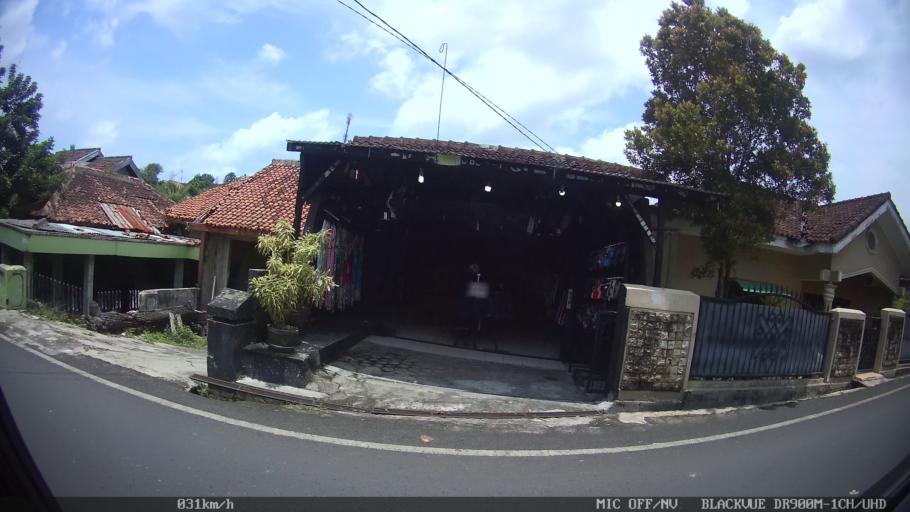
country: ID
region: Lampung
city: Bandarlampung
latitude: -5.4117
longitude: 105.2427
